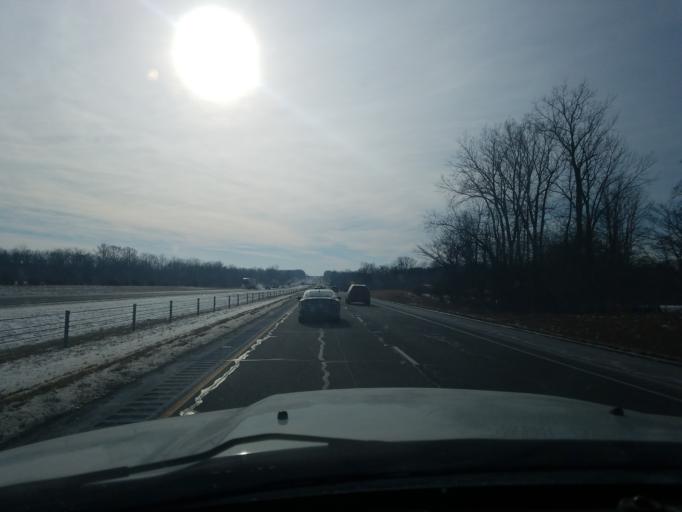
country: US
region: Indiana
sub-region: Huntington County
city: Warren
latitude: 40.7101
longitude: -85.4496
